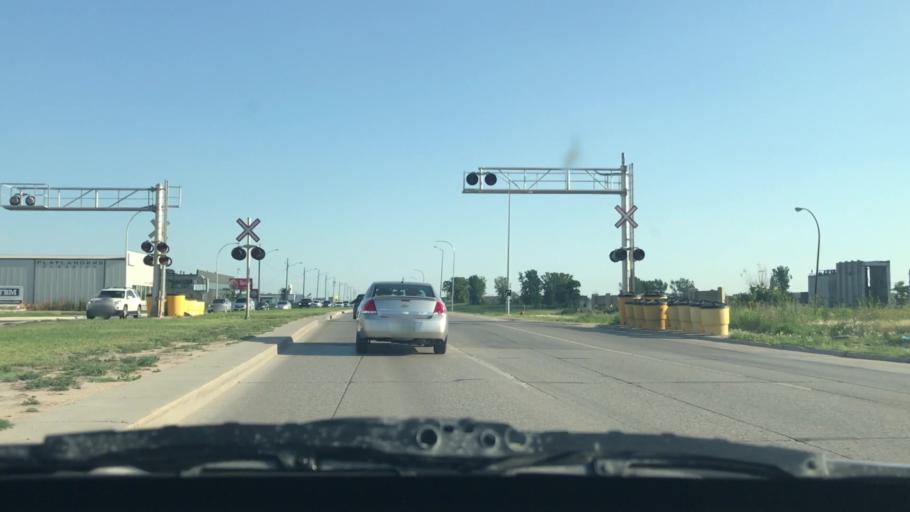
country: CA
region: Manitoba
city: Winnipeg
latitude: 49.8385
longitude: -97.2092
